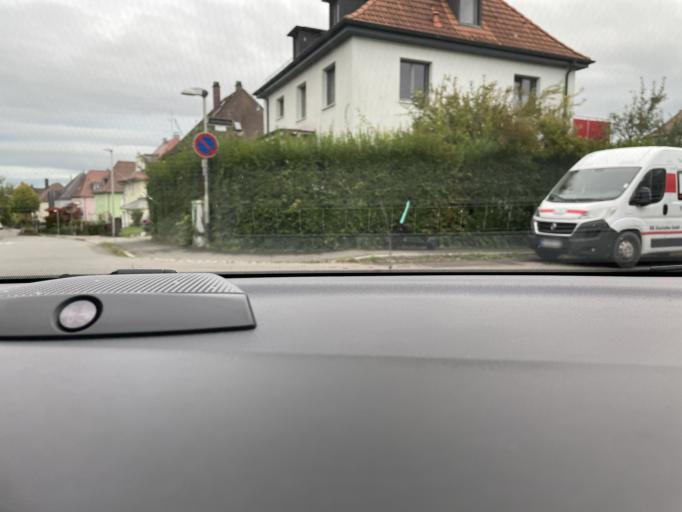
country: DE
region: Baden-Wuerttemberg
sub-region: Tuebingen Region
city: Friedrichshafen
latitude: 47.6581
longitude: 9.4597
